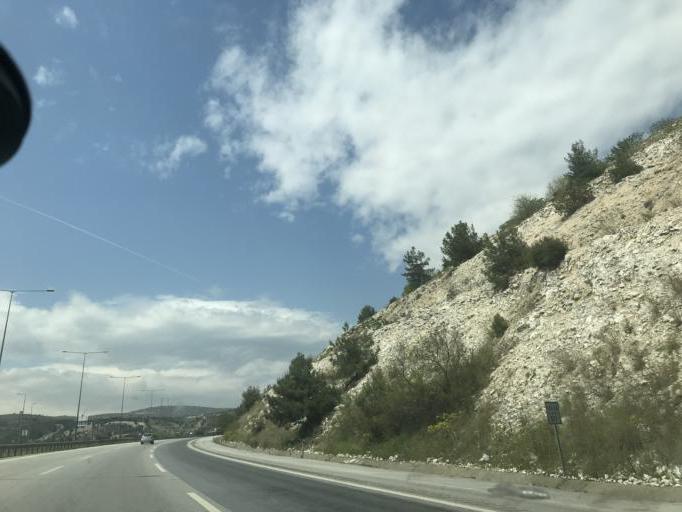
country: TR
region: Mersin
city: Tarsus
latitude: 37.1408
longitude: 34.8427
